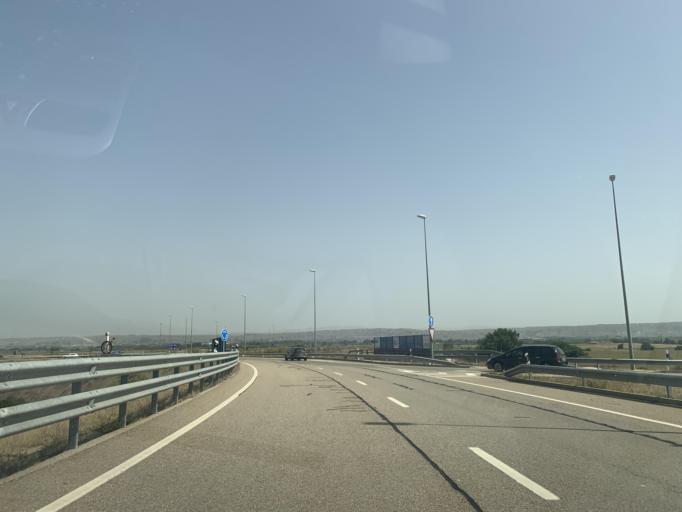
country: ES
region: Aragon
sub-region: Provincia de Zaragoza
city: Nuez de Ebro
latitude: 41.5446
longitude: -0.6950
